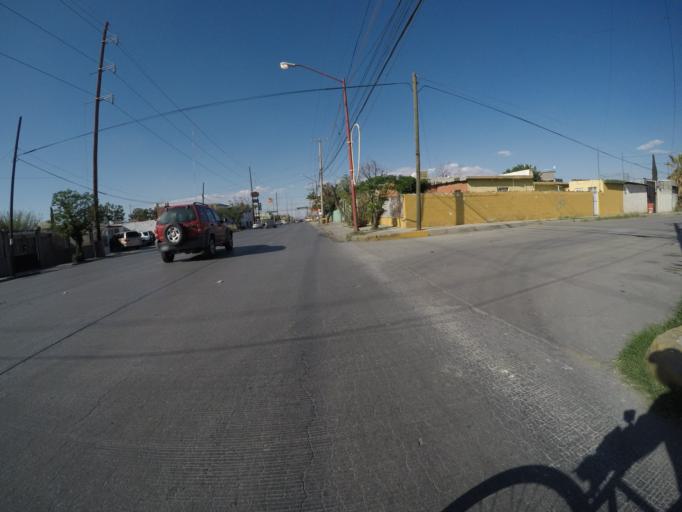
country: MX
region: Chihuahua
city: Ciudad Juarez
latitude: 31.7202
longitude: -106.4436
